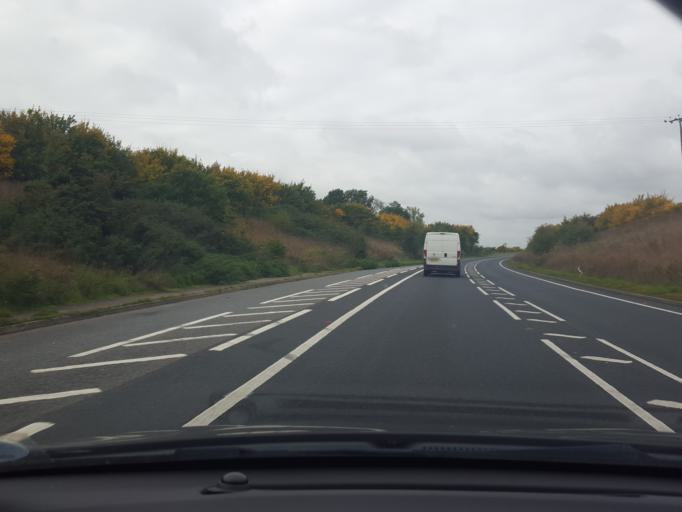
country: GB
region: England
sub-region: Essex
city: Great Bentley
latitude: 51.8466
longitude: 1.1055
